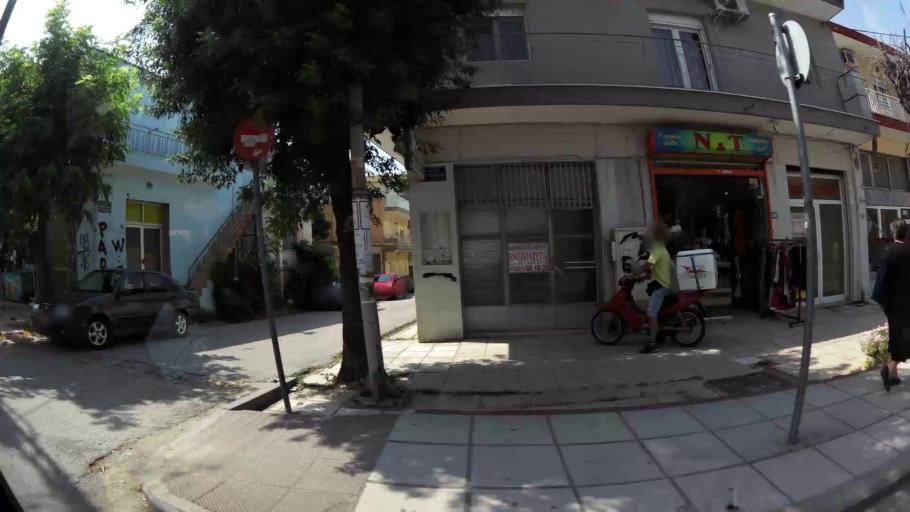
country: GR
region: Central Macedonia
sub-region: Nomos Thessalonikis
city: Ampelokipoi
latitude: 40.6665
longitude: 22.9223
